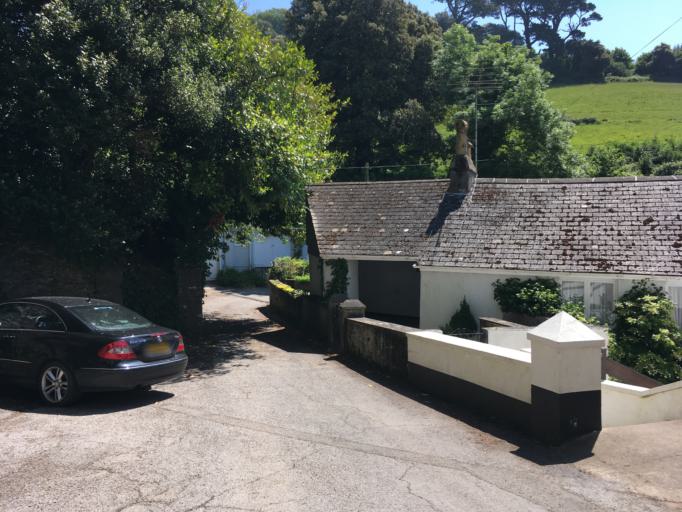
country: GB
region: England
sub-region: Devon
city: Dartmouth
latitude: 50.3461
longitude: -3.5632
